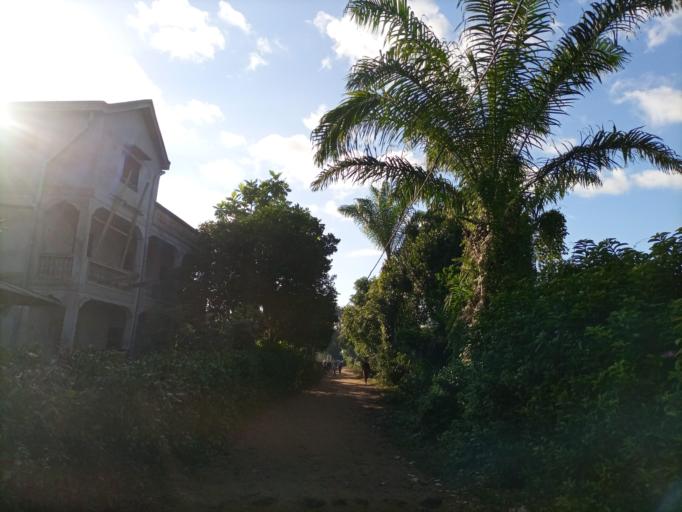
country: MG
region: Atsimo-Atsinanana
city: Vangaindrano
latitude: -23.3468
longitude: 47.6105
